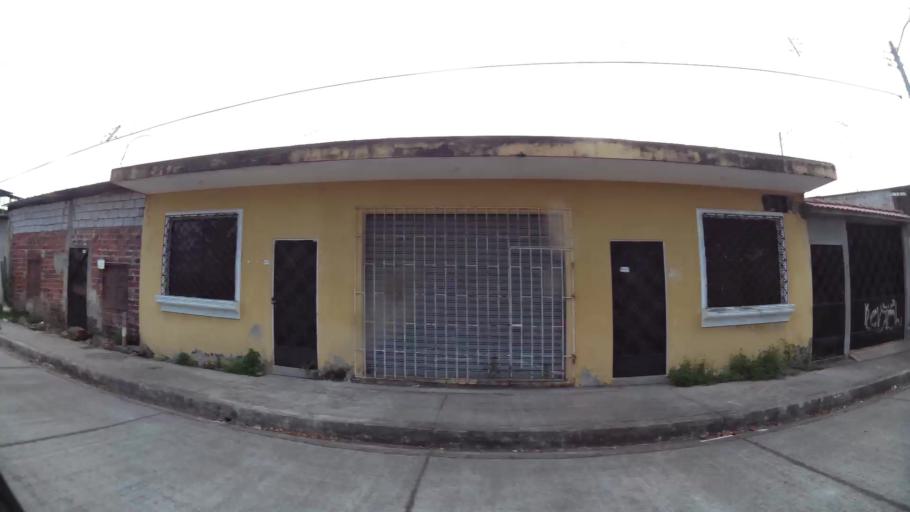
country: EC
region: Guayas
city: Eloy Alfaro
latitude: -2.0939
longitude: -79.9083
